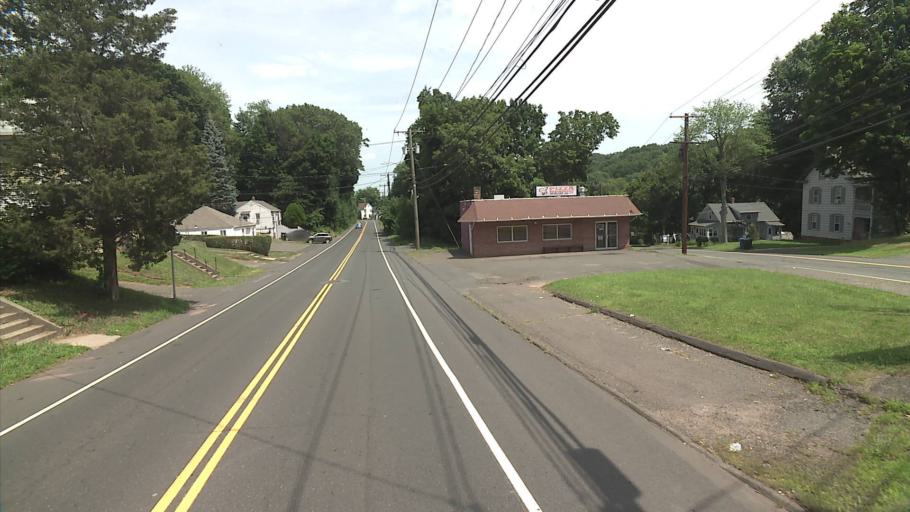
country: US
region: Connecticut
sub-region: New Haven County
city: Meriden
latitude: 41.5250
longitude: -72.8093
